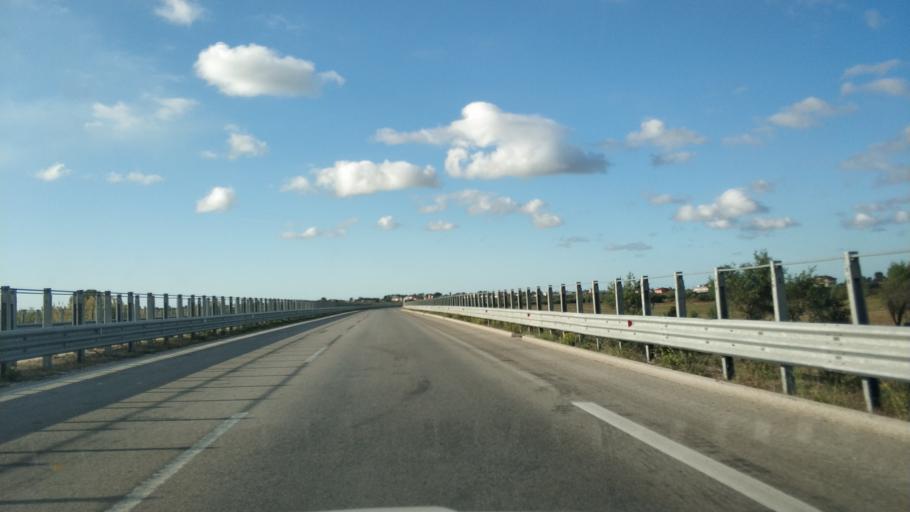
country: AL
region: Vlore
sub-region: Rrethi i Vlores
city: Novosele
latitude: 40.6303
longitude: 19.4493
